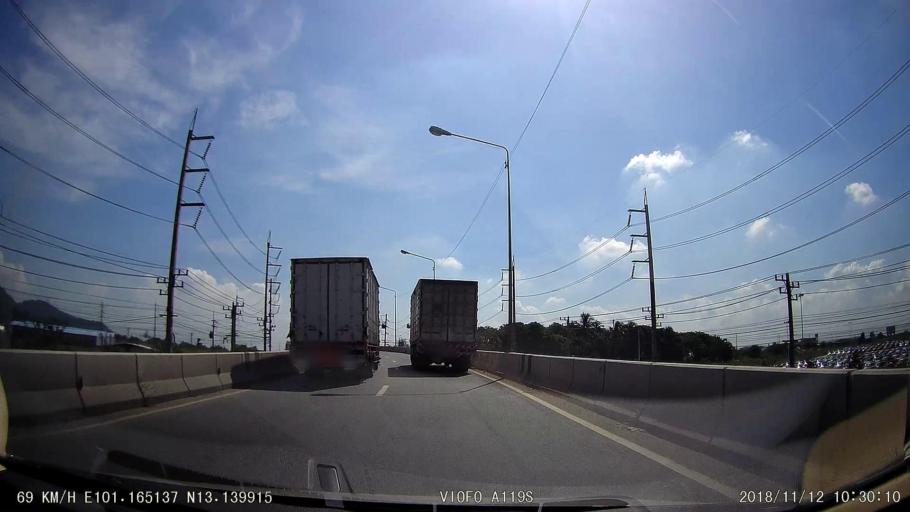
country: TH
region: Rayong
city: Pluak Daeng
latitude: 13.1308
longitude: 101.1659
